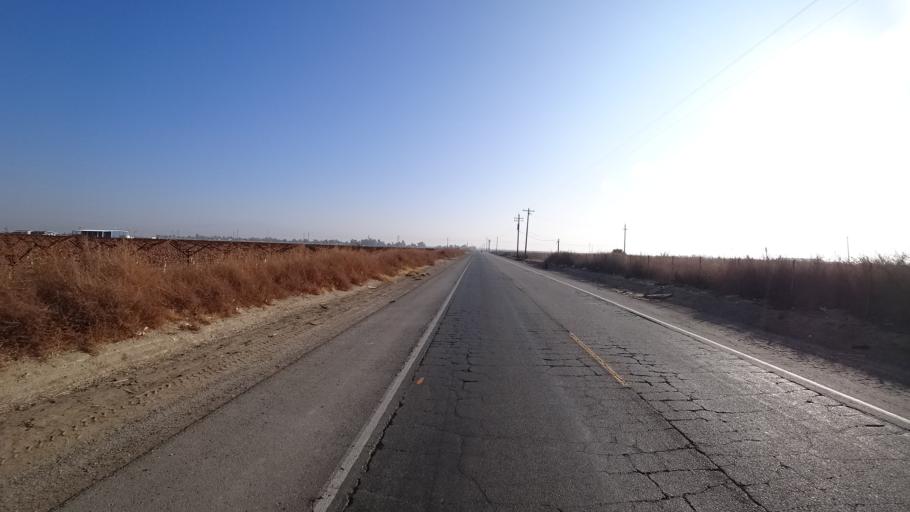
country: US
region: California
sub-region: Kern County
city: Greenfield
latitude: 35.2378
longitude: -118.9820
